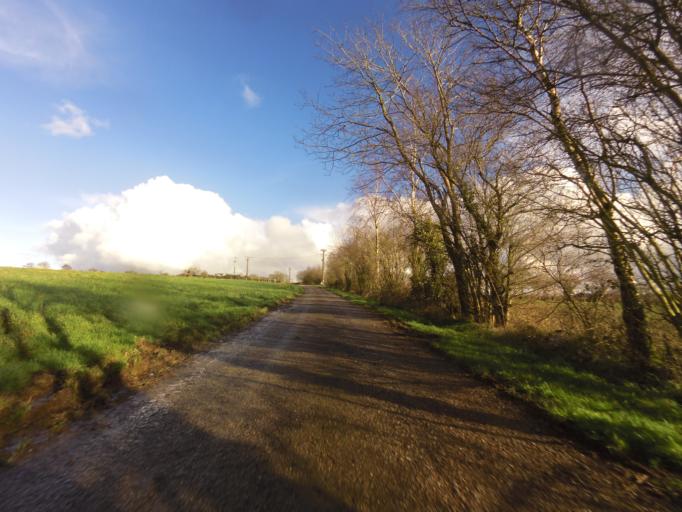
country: FR
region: Brittany
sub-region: Departement des Cotes-d'Armor
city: Gouarec
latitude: 48.1838
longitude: -3.1905
